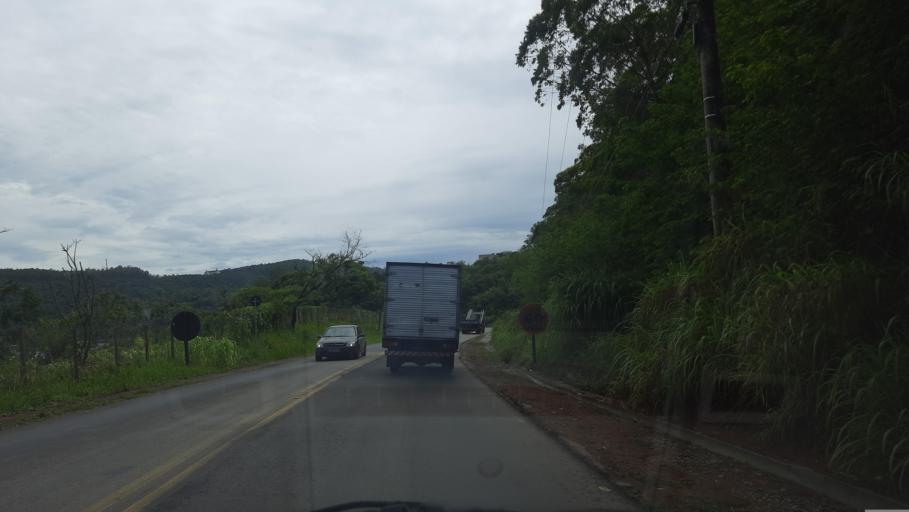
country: BR
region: Sao Paulo
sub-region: Franco Da Rocha
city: Franco da Rocha
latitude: -23.3466
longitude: -46.6632
